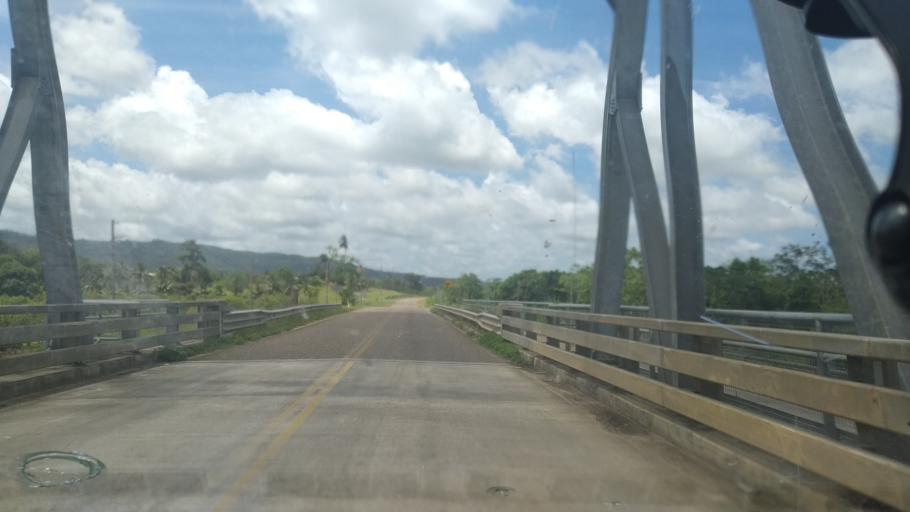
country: BZ
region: Stann Creek
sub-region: Dangriga
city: Dangriga
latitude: 16.8156
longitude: -88.3783
